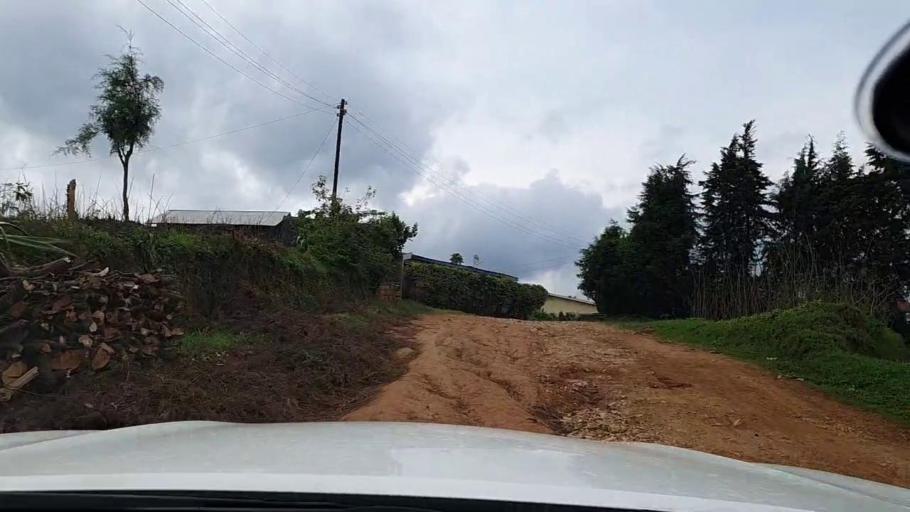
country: RW
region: Western Province
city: Kibuye
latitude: -2.1829
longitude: 29.2933
